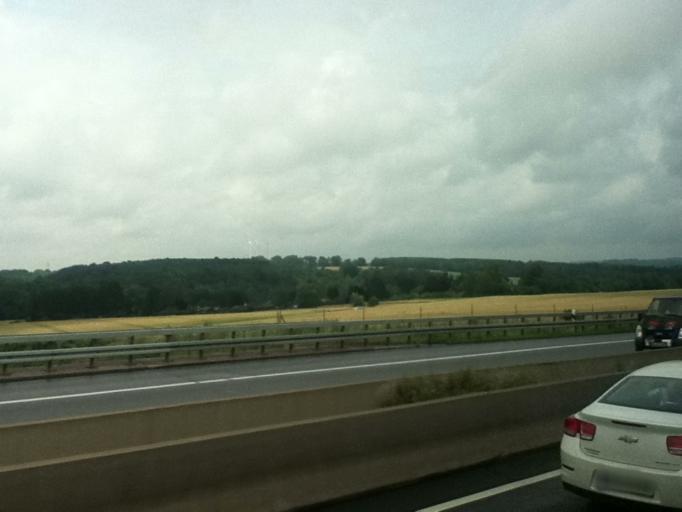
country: DE
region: Hesse
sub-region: Regierungsbezirk Giessen
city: Homberg
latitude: 50.6538
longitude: 9.0108
